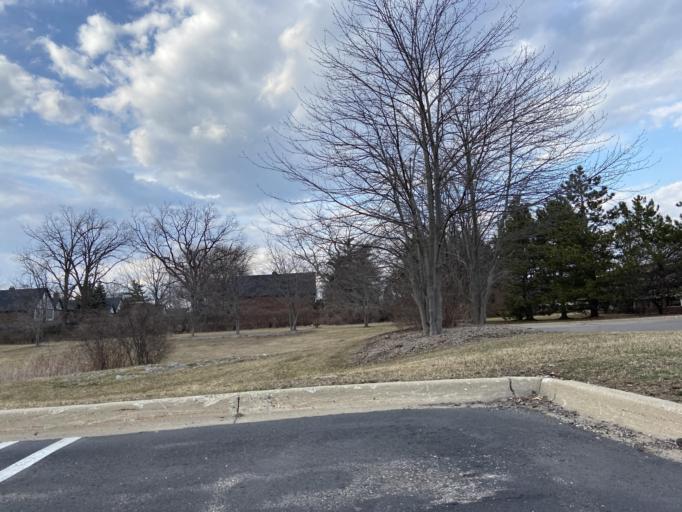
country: US
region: Michigan
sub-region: Oakland County
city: Southfield
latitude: 42.4828
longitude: -83.2467
